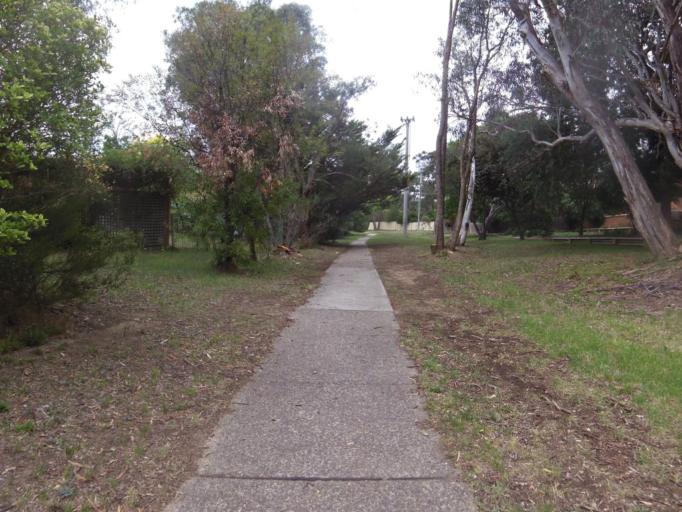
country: AU
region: Australian Capital Territory
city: Macarthur
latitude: -35.4061
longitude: 149.1285
